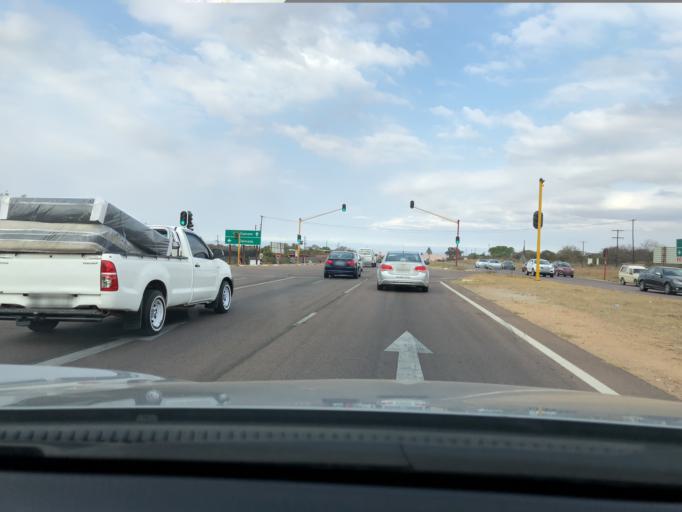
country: ZA
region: Limpopo
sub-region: Capricorn District Municipality
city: Polokwane
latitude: -23.8988
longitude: 29.5327
